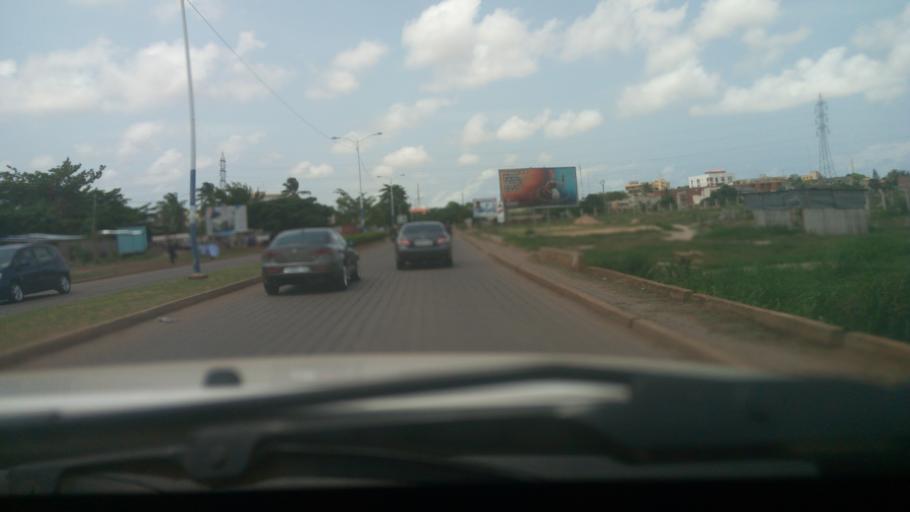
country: TG
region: Maritime
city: Lome
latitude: 6.1955
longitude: 1.2049
